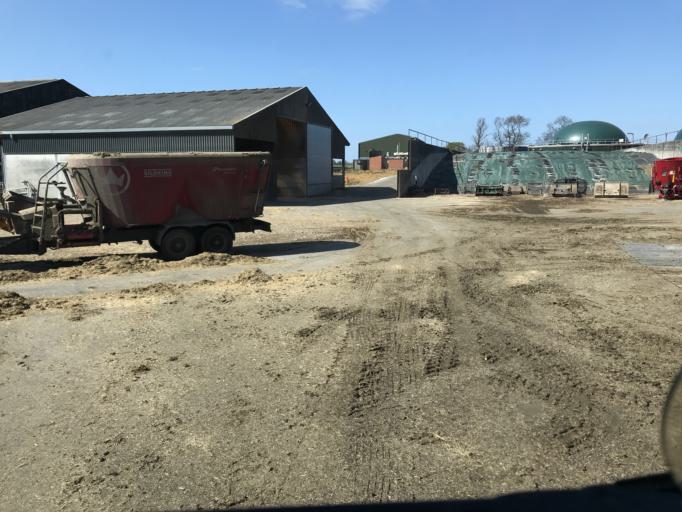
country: GB
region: England
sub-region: Cheshire East
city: Nantwich
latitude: 53.1046
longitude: -2.5386
